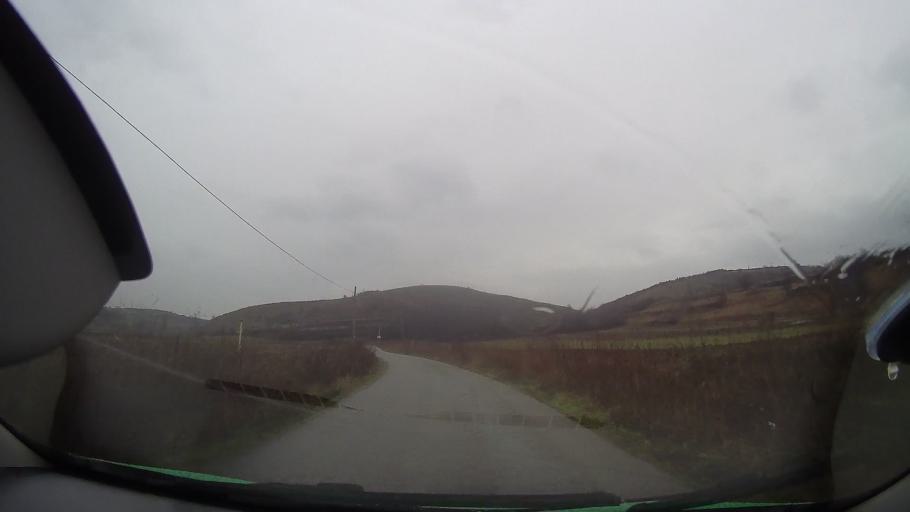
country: RO
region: Bihor
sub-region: Comuna Uileacu de Beius
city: Uileacu de Beius
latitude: 46.6924
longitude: 22.2176
